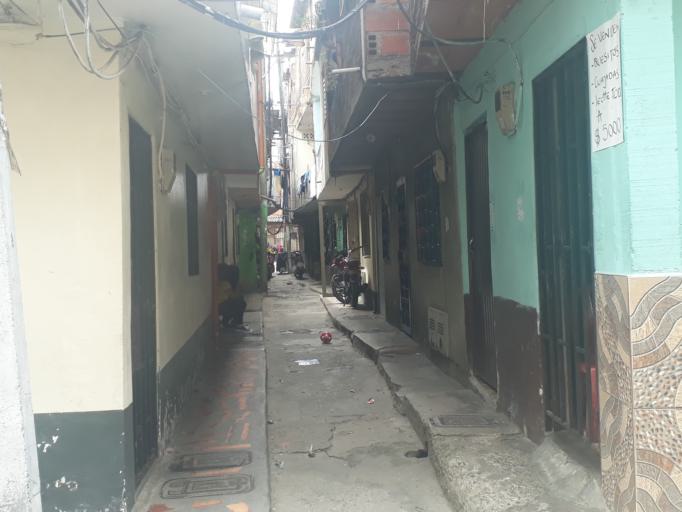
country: CO
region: Antioquia
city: Medellin
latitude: 6.2739
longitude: -75.5655
